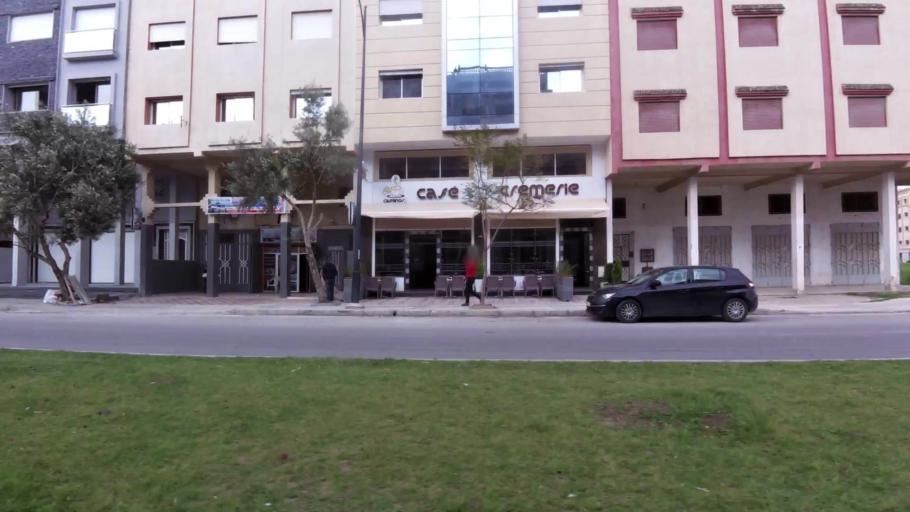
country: MA
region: Tanger-Tetouan
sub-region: Tanger-Assilah
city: Tangier
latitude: 35.7513
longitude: -5.8466
